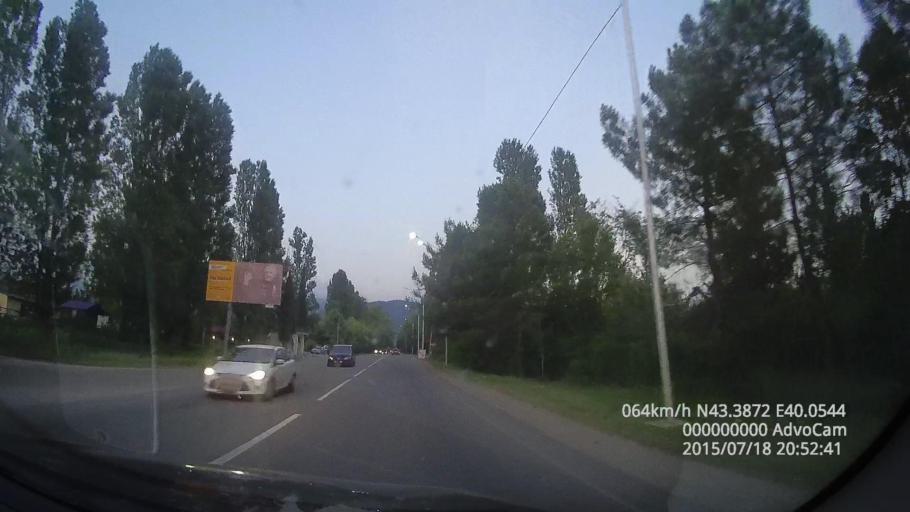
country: GE
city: Gantiadi
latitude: 43.3870
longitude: 40.0560
